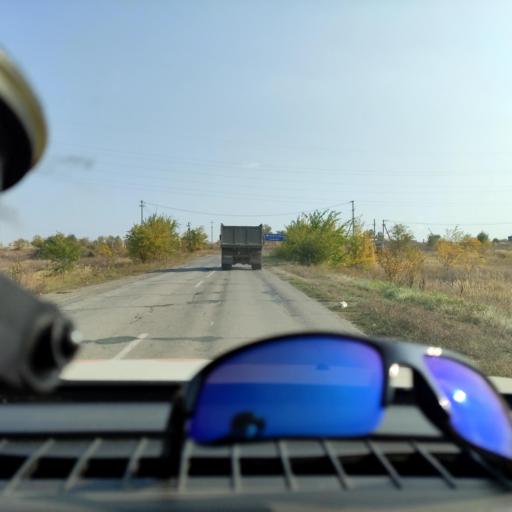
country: RU
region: Samara
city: Chapayevsk
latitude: 53.0000
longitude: 49.7652
